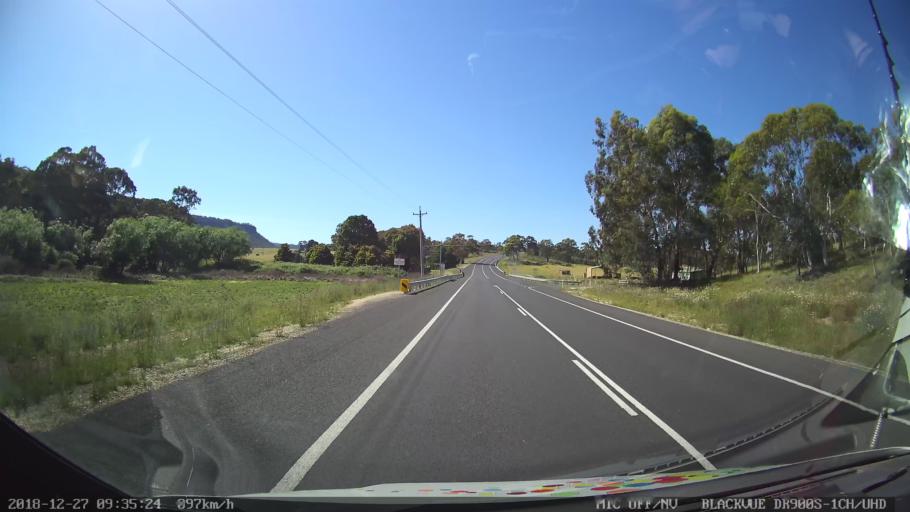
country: AU
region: New South Wales
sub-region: Lithgow
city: Portland
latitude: -33.2381
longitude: 150.0302
